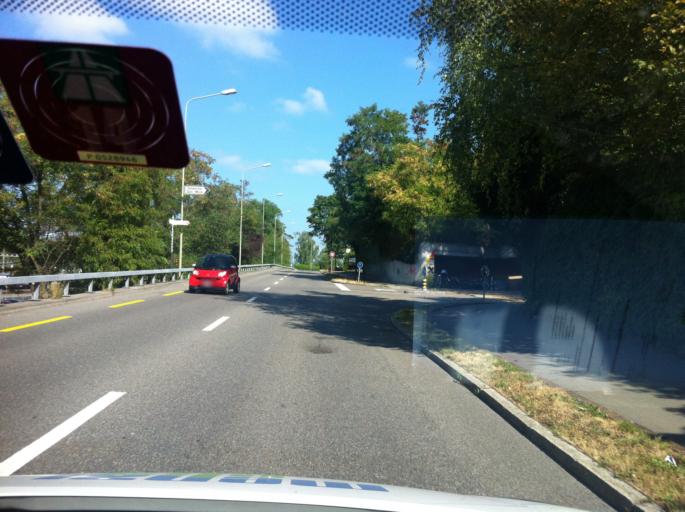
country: CH
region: Zurich
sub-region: Bezirk Buelach
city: Bulach
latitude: 47.5232
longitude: 8.5394
